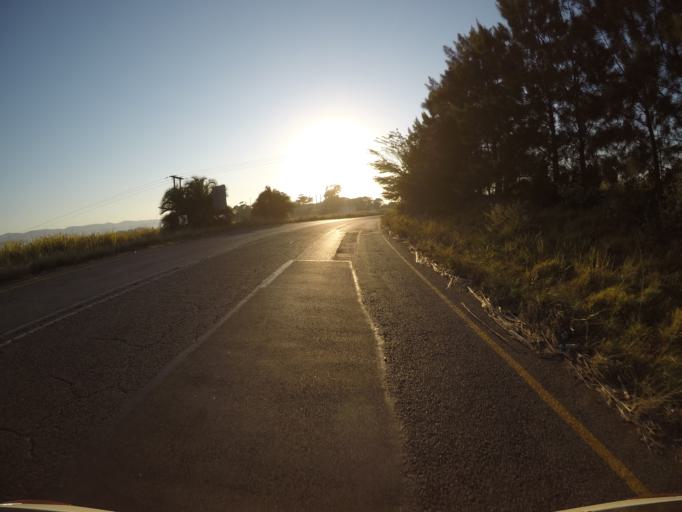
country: ZA
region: KwaZulu-Natal
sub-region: uThungulu District Municipality
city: Eshowe
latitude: -28.9466
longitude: 31.6801
